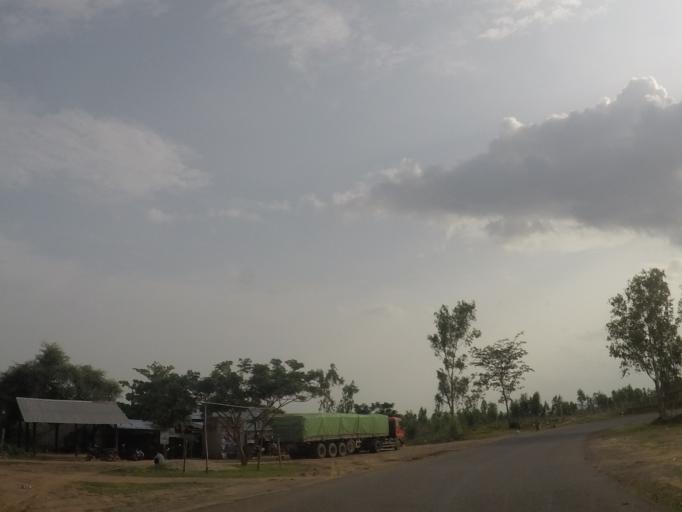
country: MM
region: Mandalay
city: Meiktila
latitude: 20.5230
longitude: 95.6572
